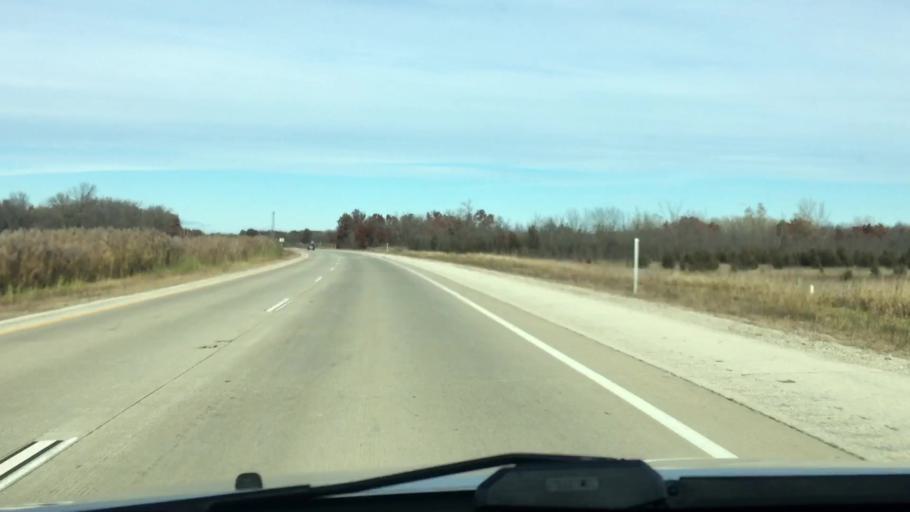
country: US
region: Wisconsin
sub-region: Brown County
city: Bellevue
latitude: 44.5844
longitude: -87.8679
